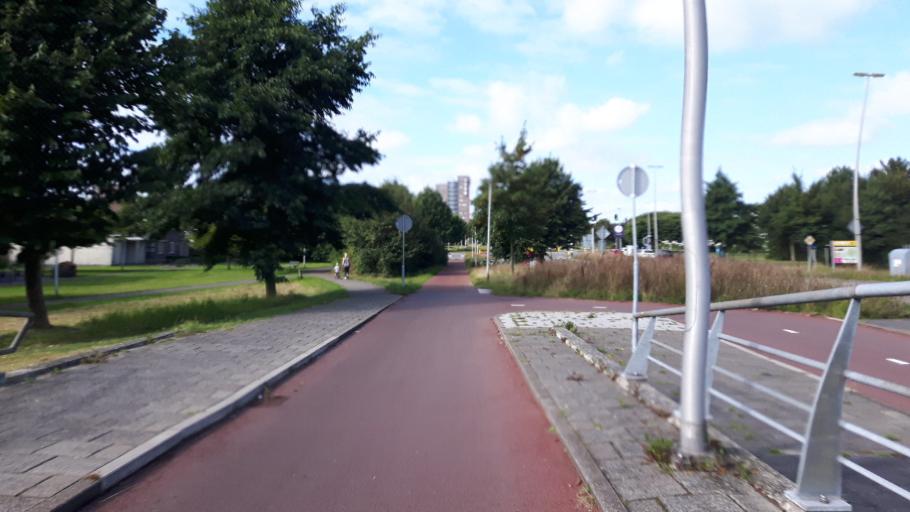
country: NL
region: North Holland
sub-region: Gemeente Purmerend
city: Purmerend
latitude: 52.4962
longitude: 4.9462
